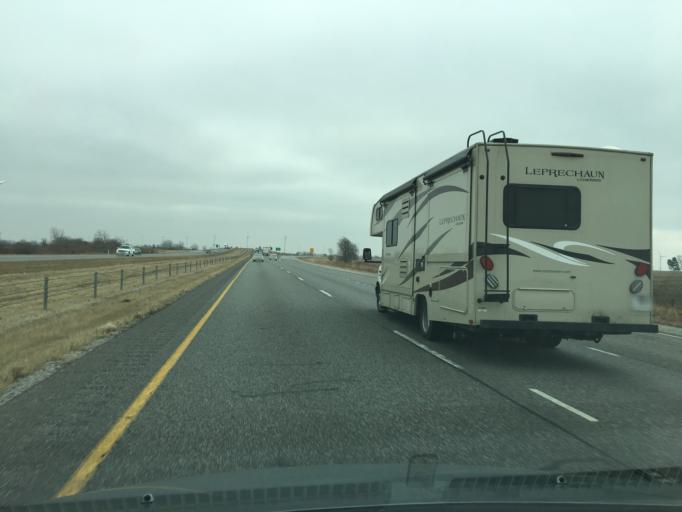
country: US
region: Indiana
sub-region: White County
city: Wolcott
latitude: 40.6711
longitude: -87.0478
